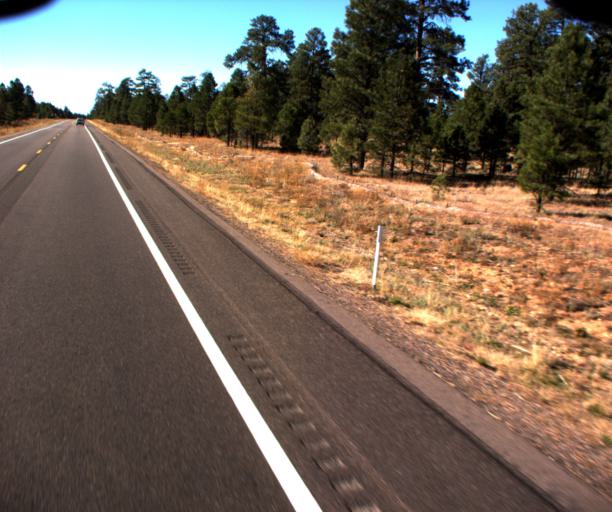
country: US
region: Arizona
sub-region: Apache County
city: Saint Michaels
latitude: 35.6839
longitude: -109.2301
